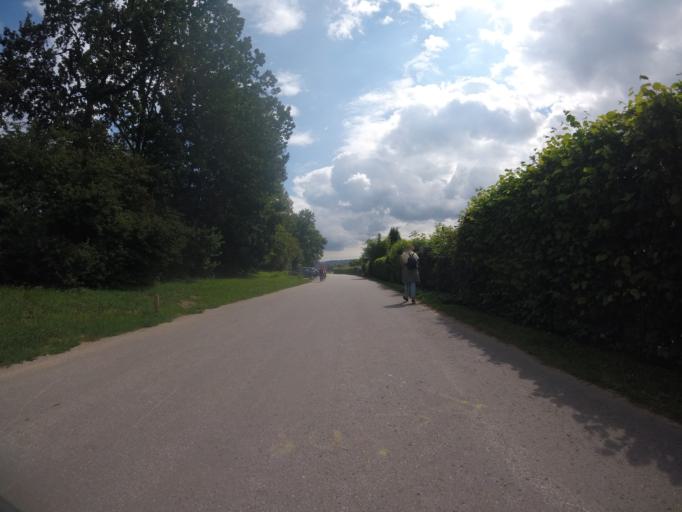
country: DE
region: Baden-Wuerttemberg
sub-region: Regierungsbezirk Stuttgart
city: Winterbach
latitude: 48.8027
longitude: 9.4594
